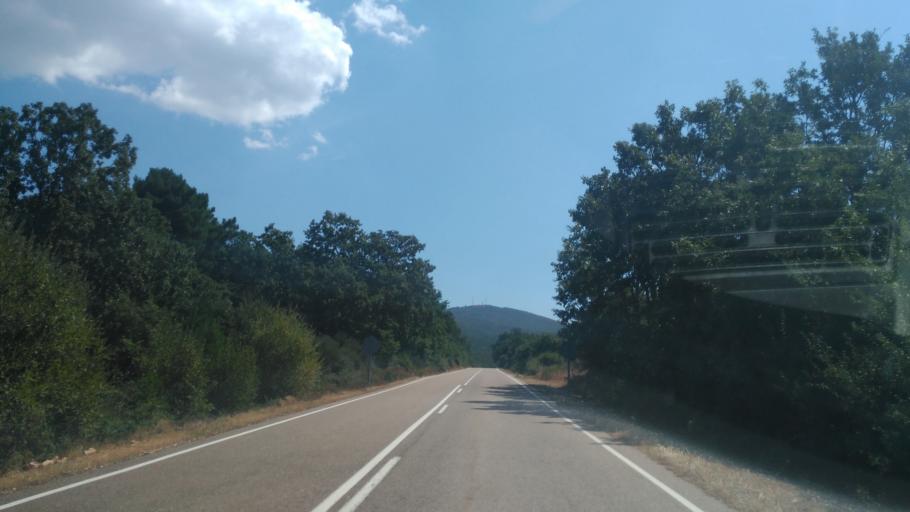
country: ES
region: Castille and Leon
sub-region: Provincia de Salamanca
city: Cereceda de la Sierra
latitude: 40.5602
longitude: -6.0781
